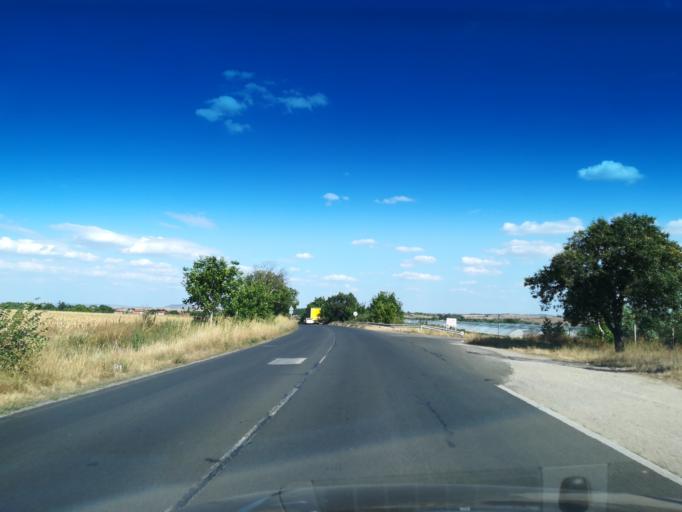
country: BG
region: Stara Zagora
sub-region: Obshtina Chirpan
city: Chirpan
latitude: 42.0585
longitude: 25.2506
